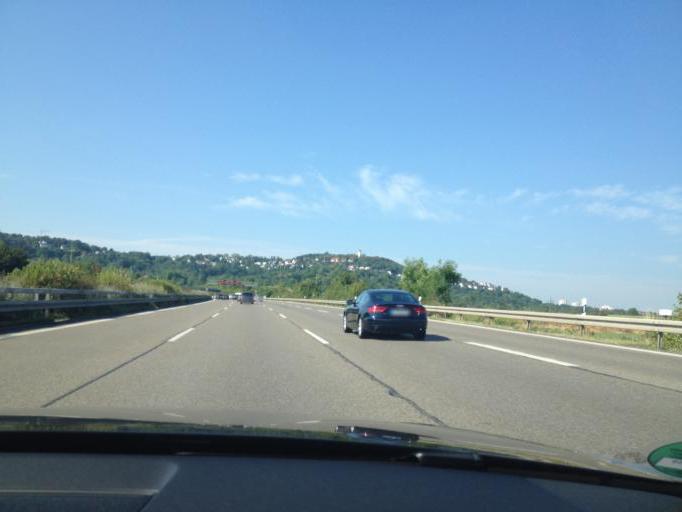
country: DE
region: Baden-Wuerttemberg
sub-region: Regierungsbezirk Stuttgart
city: Gerlingen
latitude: 48.8078
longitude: 9.0462
